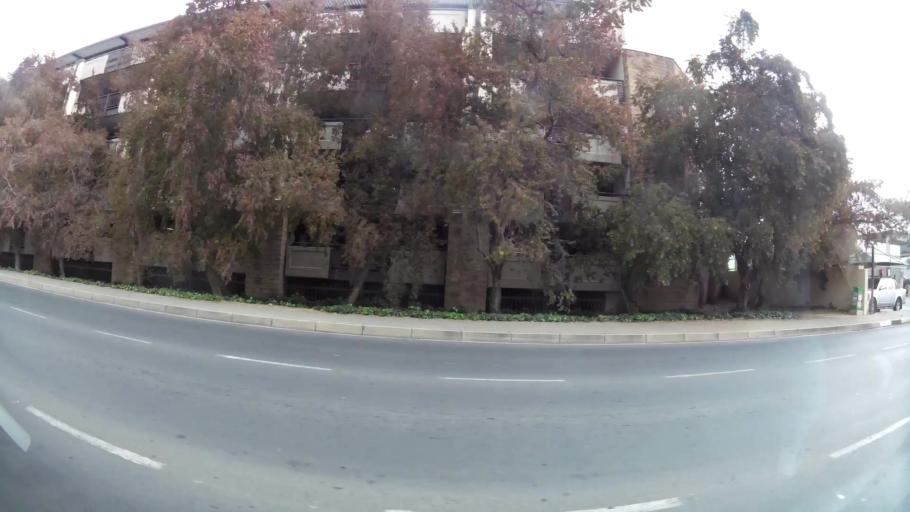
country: ZA
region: Orange Free State
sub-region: Mangaung Metropolitan Municipality
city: Bloemfontein
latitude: -29.1088
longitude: 26.2024
